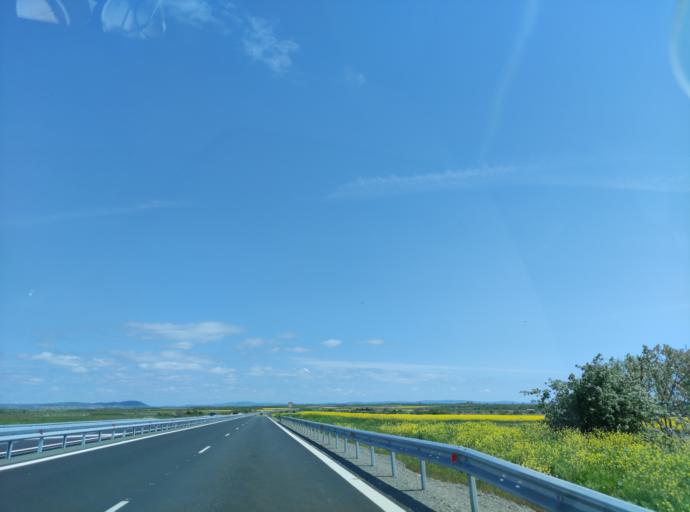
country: BG
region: Burgas
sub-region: Obshtina Pomorie
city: Pomorie
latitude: 42.5621
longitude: 27.5706
